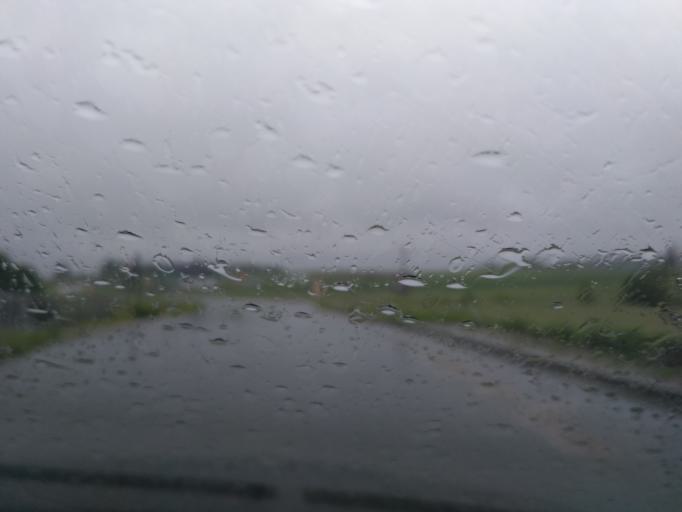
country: PL
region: Subcarpathian Voivodeship
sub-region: Powiat jasielski
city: Debowiec
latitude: 49.6710
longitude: 21.4530
